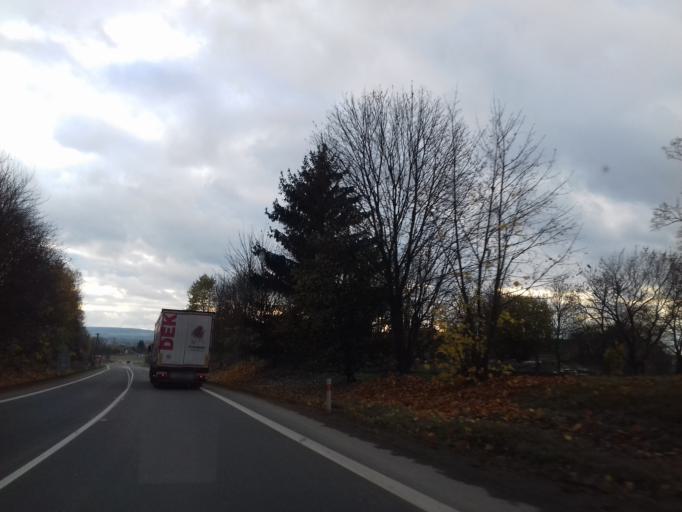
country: CZ
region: Pardubicky
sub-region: Okres Svitavy
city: Svitavy
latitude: 49.7579
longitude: 16.4870
